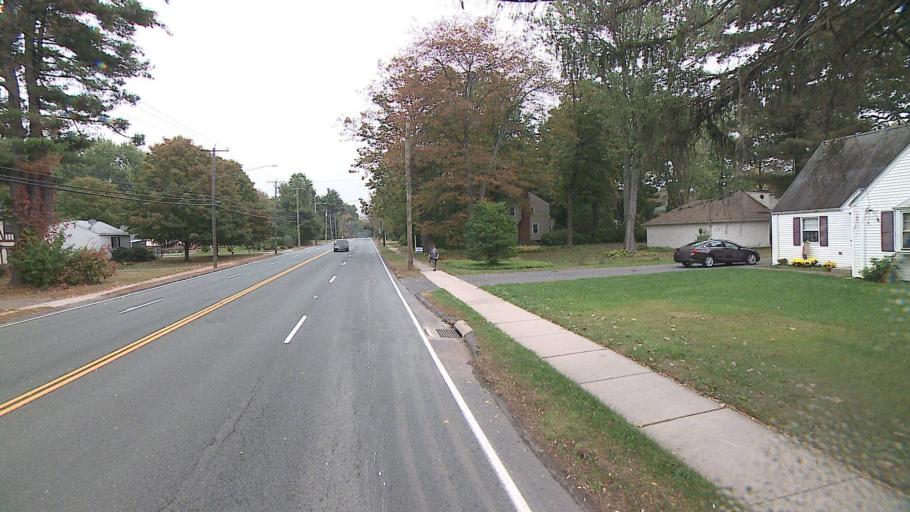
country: US
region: Connecticut
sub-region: Hartford County
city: West Hartford
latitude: 41.7865
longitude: -72.7388
